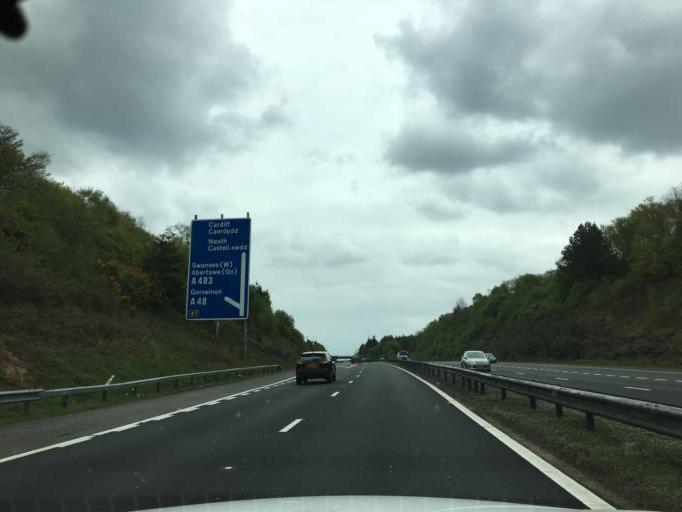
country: GB
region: Wales
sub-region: City and County of Swansea
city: Pontlliw
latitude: 51.6774
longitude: -4.0041
